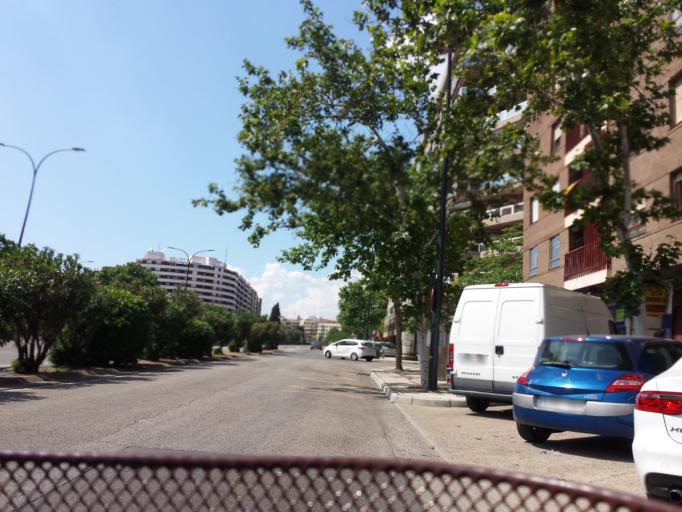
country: ES
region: Aragon
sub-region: Provincia de Zaragoza
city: Zaragoza
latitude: 41.6432
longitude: -0.8759
